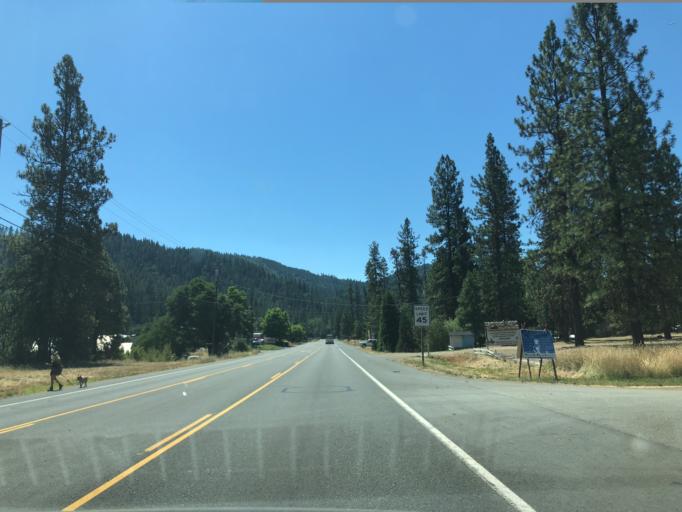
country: US
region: California
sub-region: Trinity County
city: Weaverville
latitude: 40.7189
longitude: -122.9276
